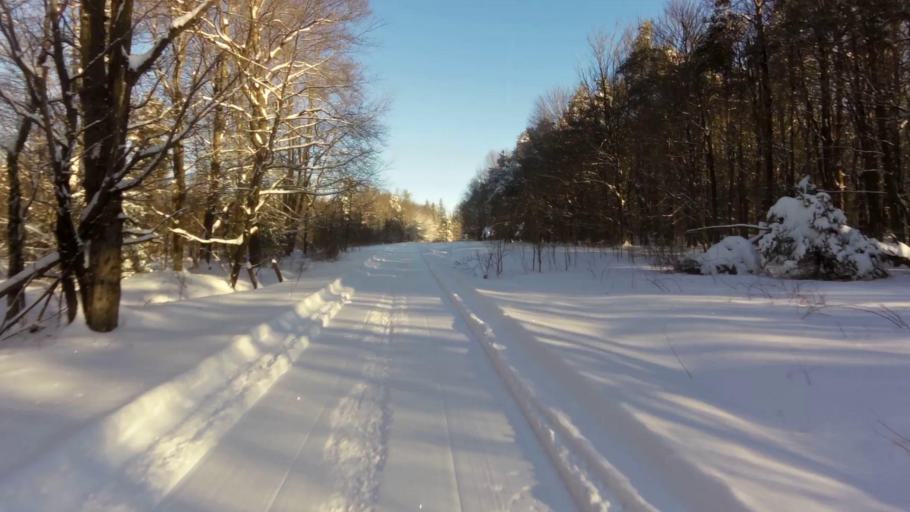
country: US
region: New York
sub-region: Chautauqua County
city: Falconer
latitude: 42.2377
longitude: -79.2178
